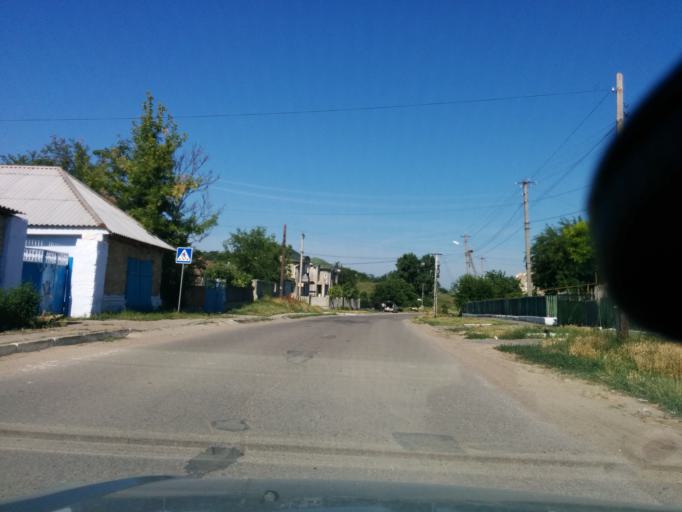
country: MD
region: Chisinau
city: Vadul lui Voda
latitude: 47.0628
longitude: 28.9994
